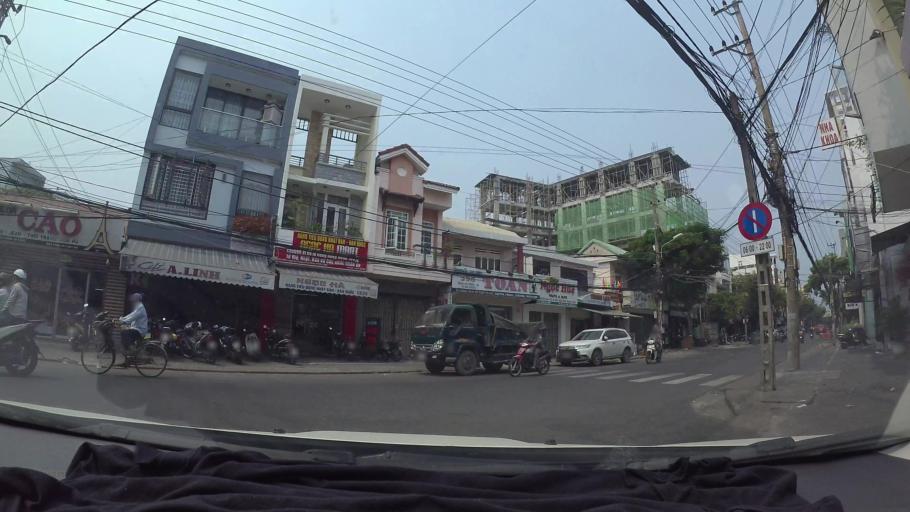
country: VN
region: Da Nang
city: Da Nang
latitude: 16.0511
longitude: 108.2161
